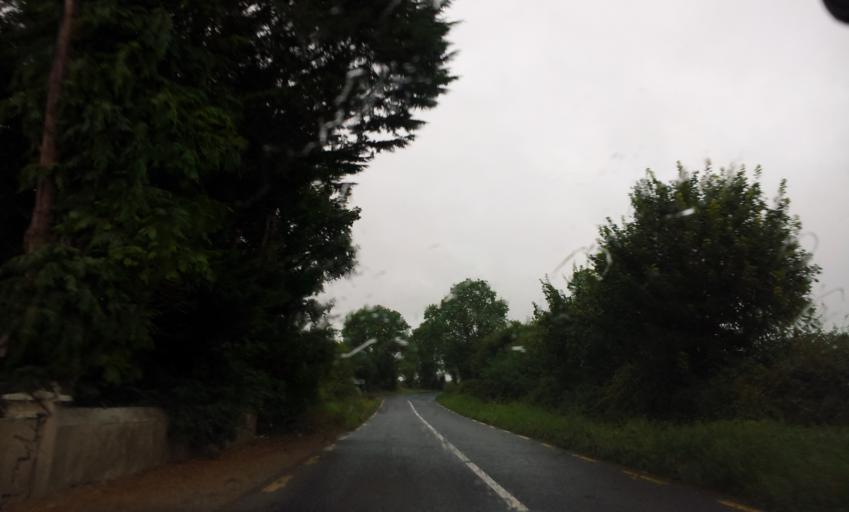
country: IE
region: Munster
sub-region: County Cork
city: Mallow
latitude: 52.1603
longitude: -8.5925
